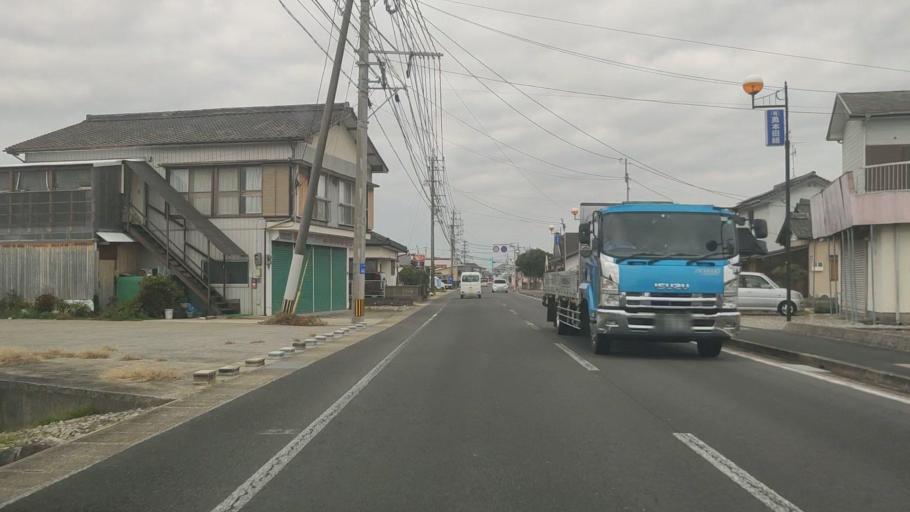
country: JP
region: Nagasaki
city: Shimabara
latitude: 32.8644
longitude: 130.3223
